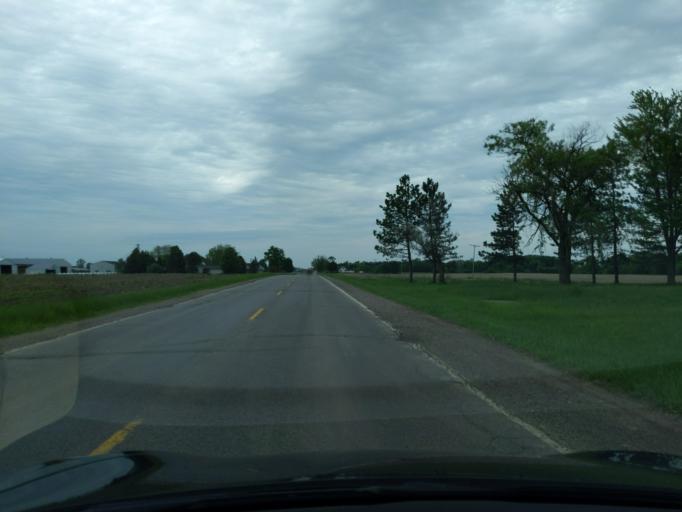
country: US
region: Michigan
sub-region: Ingham County
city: Mason
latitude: 42.6314
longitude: -84.3639
